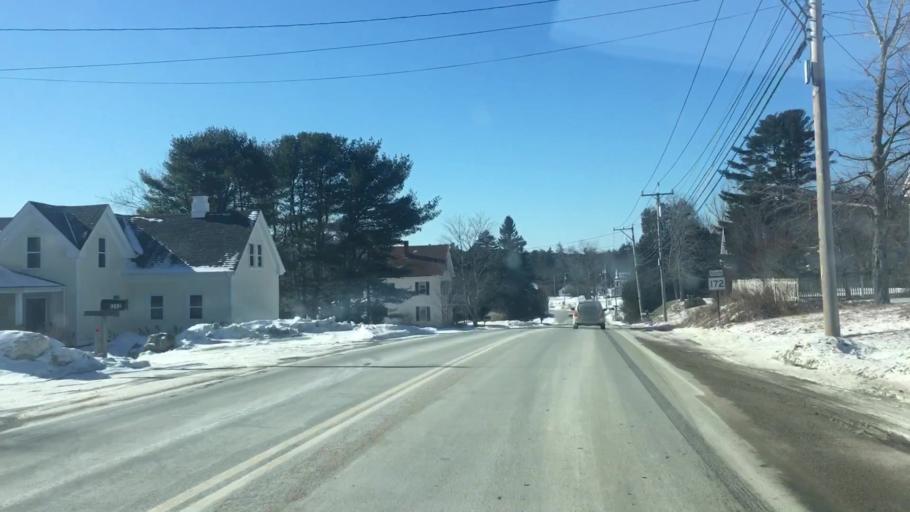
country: US
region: Maine
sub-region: Hancock County
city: Surry
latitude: 44.4954
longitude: -68.5024
